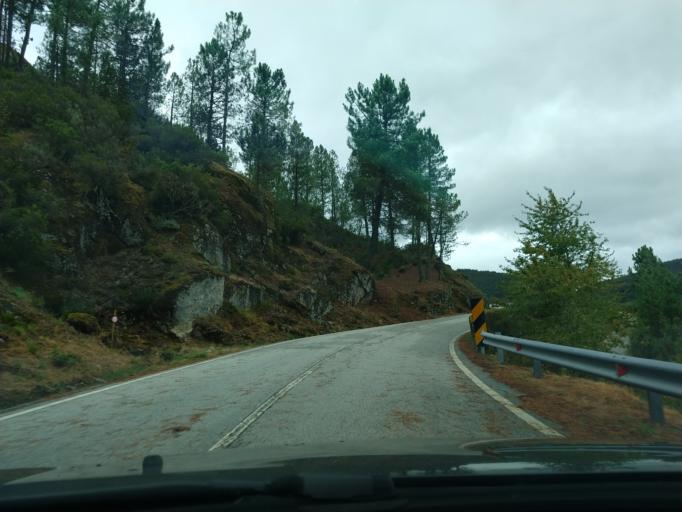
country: PT
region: Guarda
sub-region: Seia
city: Seia
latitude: 40.3216
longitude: -7.6835
